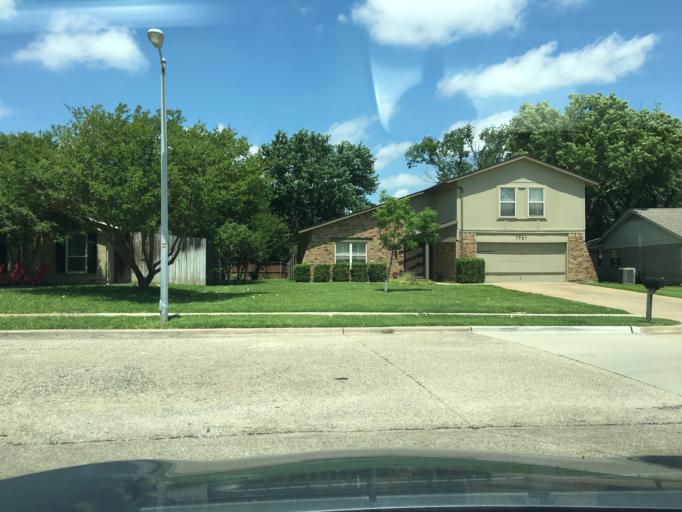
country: US
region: Texas
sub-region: Dallas County
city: Richardson
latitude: 32.9697
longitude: -96.6903
